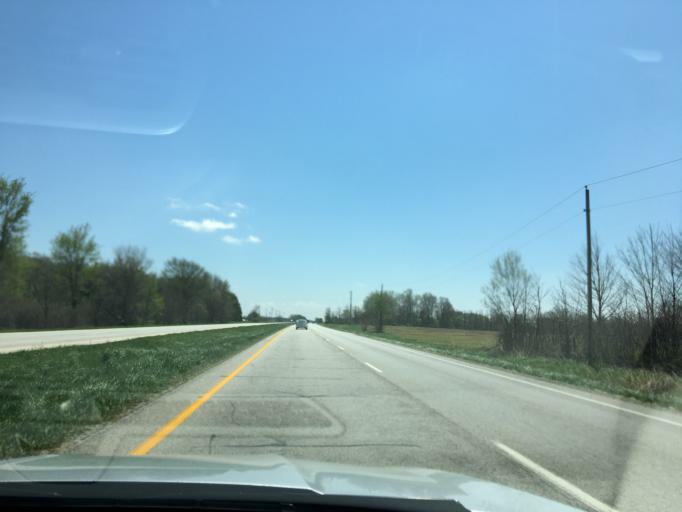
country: US
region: Indiana
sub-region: Boone County
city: Thorntown
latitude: 40.2095
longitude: -86.6501
